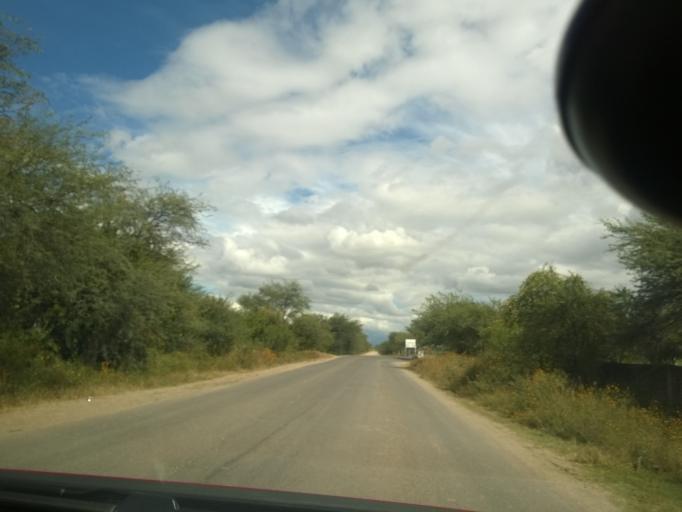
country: MX
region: Guanajuato
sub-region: Leon
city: Plan Guanajuato (La Sandia)
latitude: 20.9622
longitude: -101.6361
